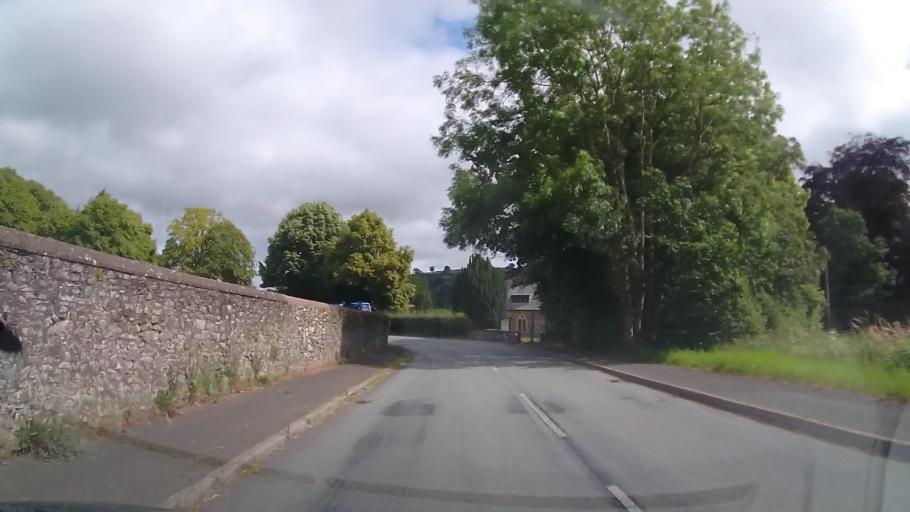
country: GB
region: Wales
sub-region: Sir Powys
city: Llanfechain
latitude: 52.8096
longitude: -3.2061
